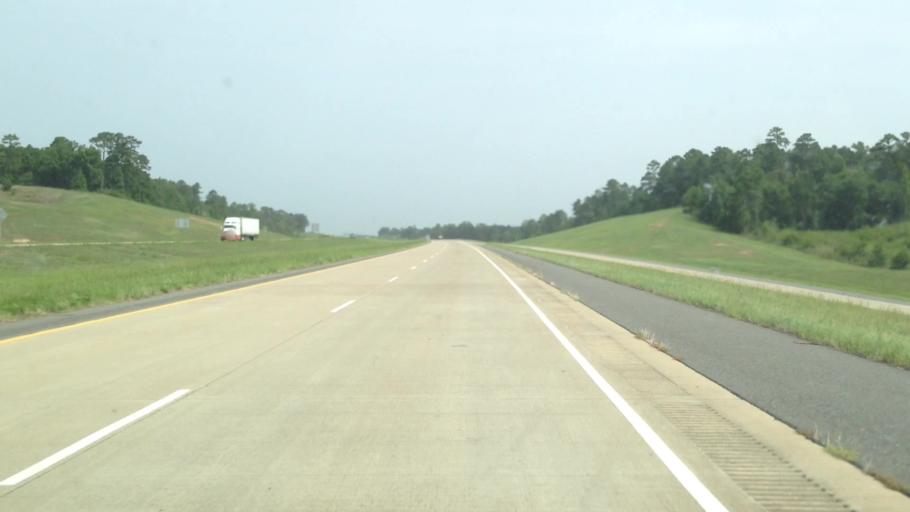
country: US
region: Louisiana
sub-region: Caddo Parish
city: Vivian
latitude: 32.9447
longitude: -93.8978
